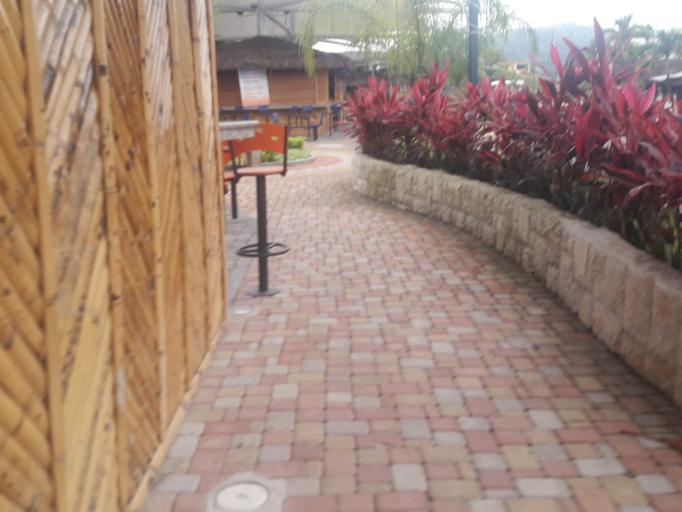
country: EC
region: Napo
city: Tena
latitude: -0.9905
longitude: -77.8142
